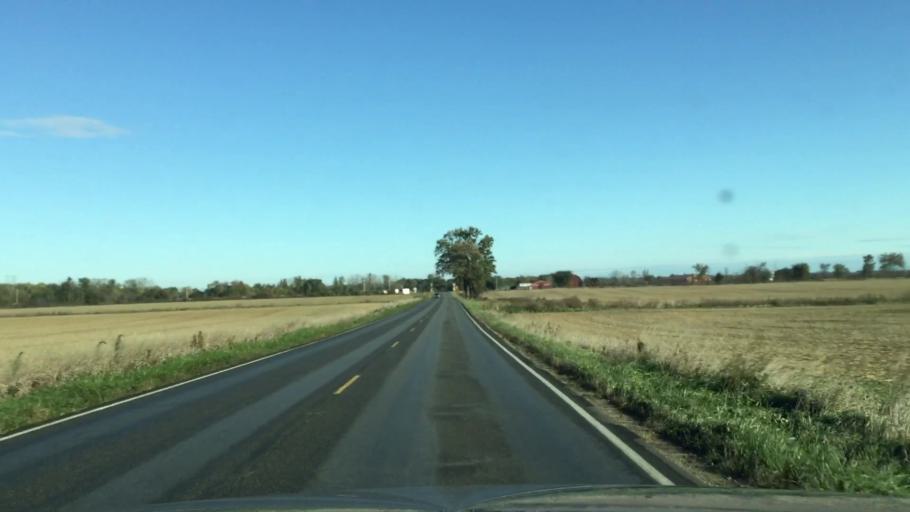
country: US
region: Michigan
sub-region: Shiawassee County
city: Durand
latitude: 42.9145
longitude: -83.9484
